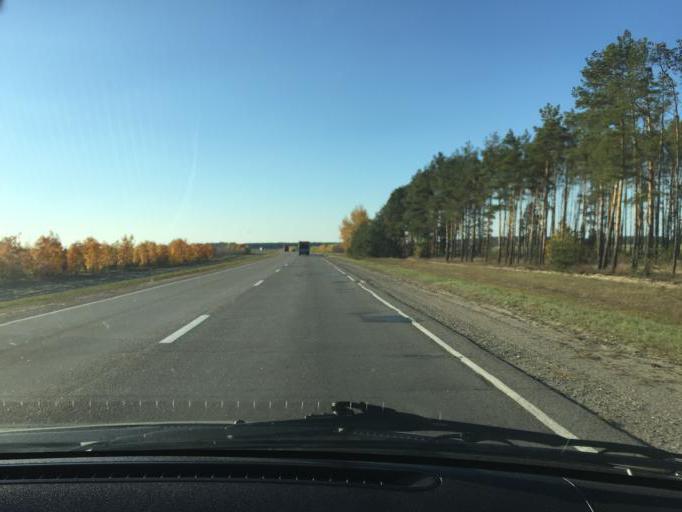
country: BY
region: Brest
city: Luninyets
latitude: 52.2733
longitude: 26.9842
